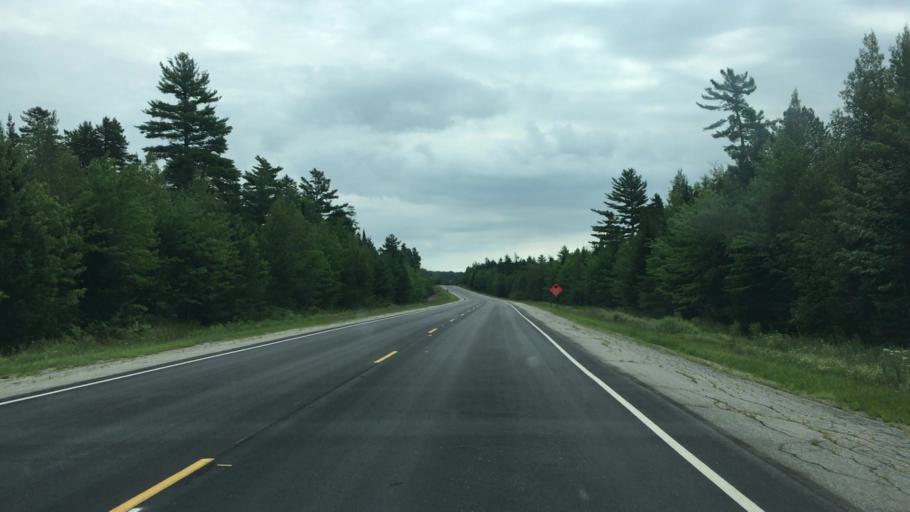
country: US
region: Maine
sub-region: Washington County
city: Addison
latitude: 44.9063
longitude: -67.8248
